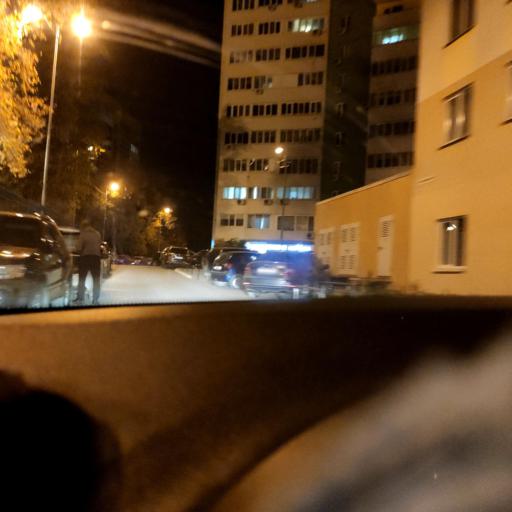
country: RU
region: Samara
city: Samara
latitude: 53.1941
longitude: 50.2056
